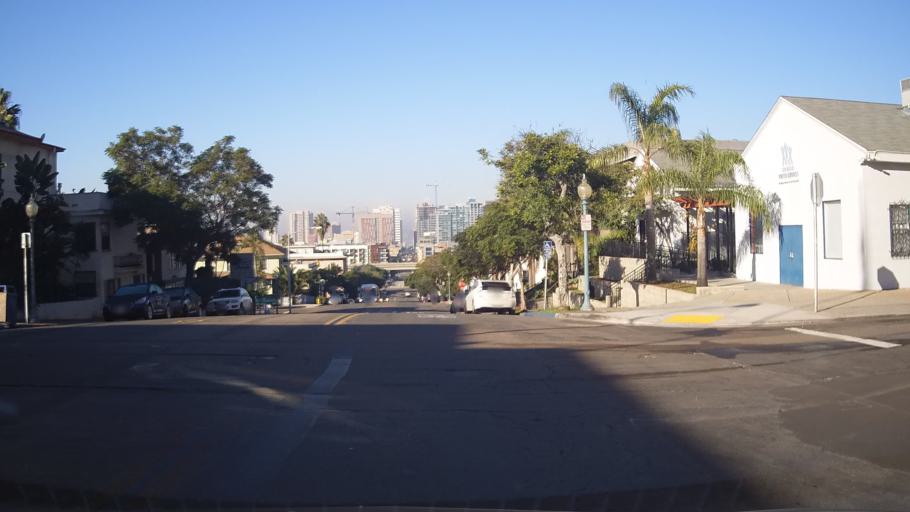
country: US
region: California
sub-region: San Diego County
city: San Diego
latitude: 32.7159
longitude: -117.1430
